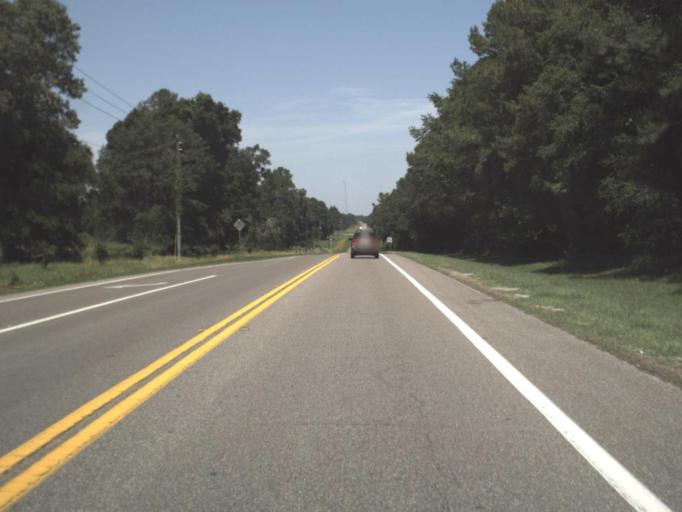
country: US
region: Florida
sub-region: Suwannee County
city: Live Oak
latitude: 30.2648
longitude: -82.9171
